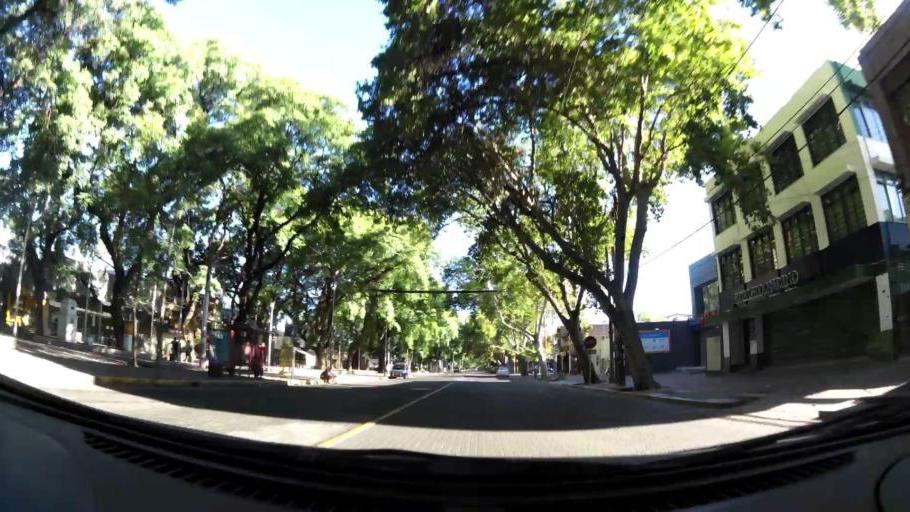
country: AR
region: Mendoza
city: Mendoza
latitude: -32.8779
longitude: -68.8361
